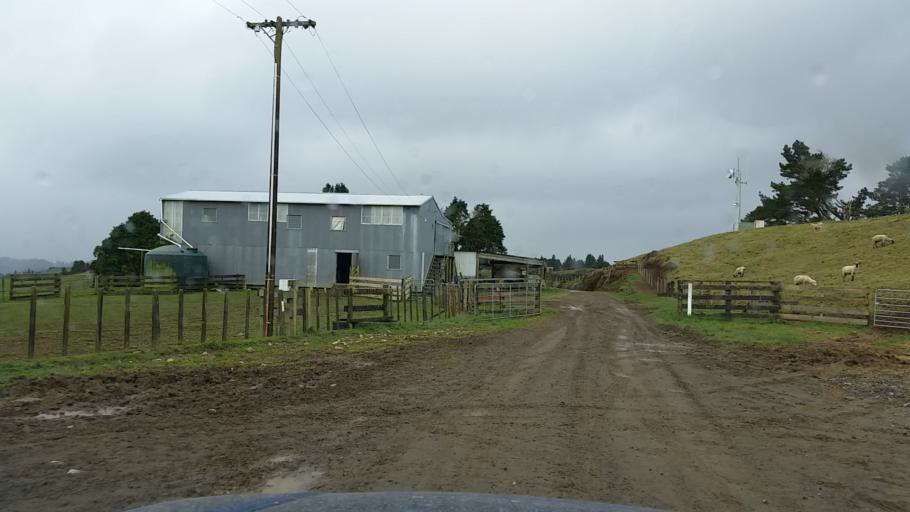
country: NZ
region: Taranaki
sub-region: South Taranaki District
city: Eltham
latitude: -39.1661
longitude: 174.6279
